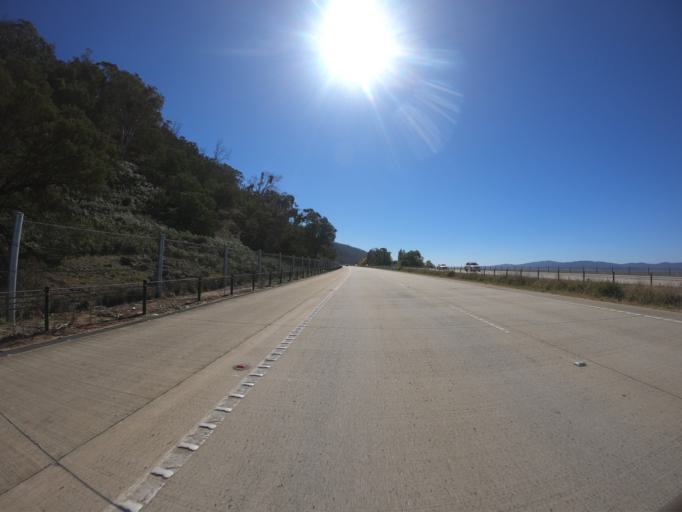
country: AU
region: New South Wales
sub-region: Yass Valley
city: Gundaroo
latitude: -35.0760
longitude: 149.3745
